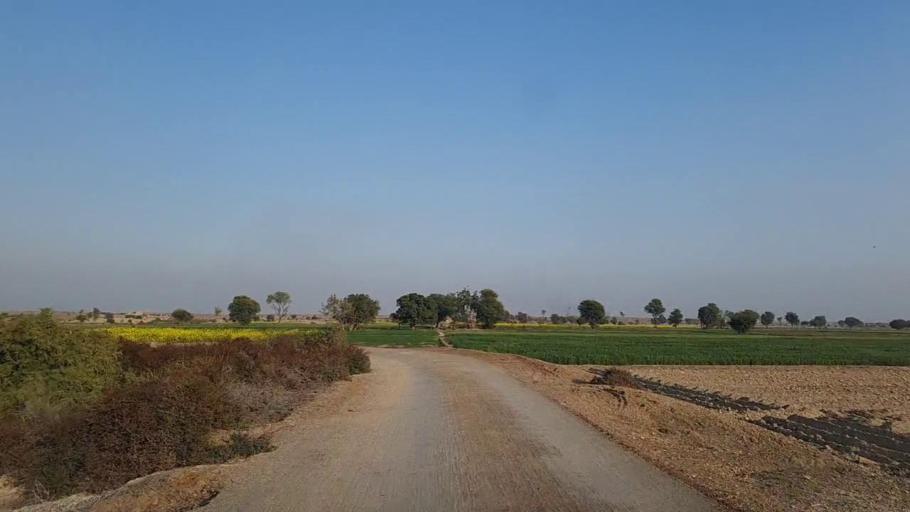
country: PK
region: Sindh
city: Jam Sahib
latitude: 26.3860
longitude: 68.5399
